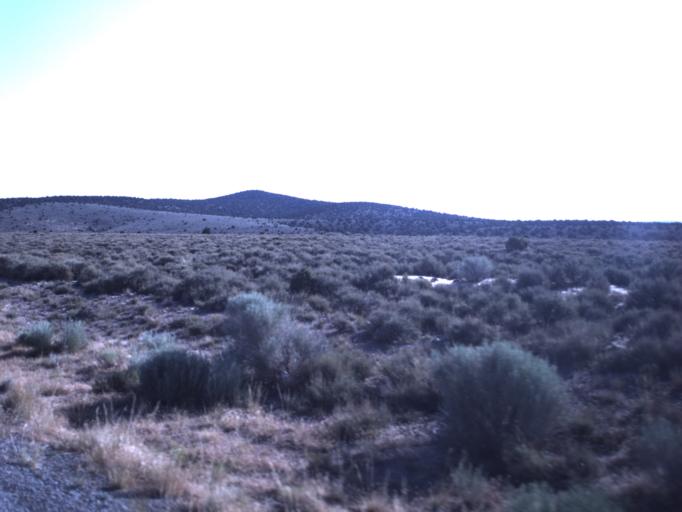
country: US
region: Utah
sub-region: Iron County
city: Parowan
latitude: 38.0183
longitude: -112.9980
